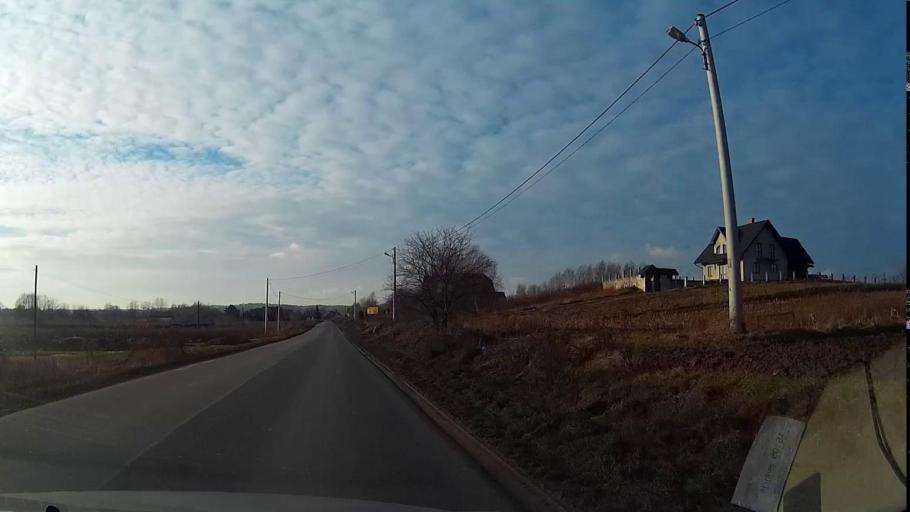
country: PL
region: Lesser Poland Voivodeship
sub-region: Powiat krakowski
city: Mnikow
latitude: 50.0589
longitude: 19.7503
